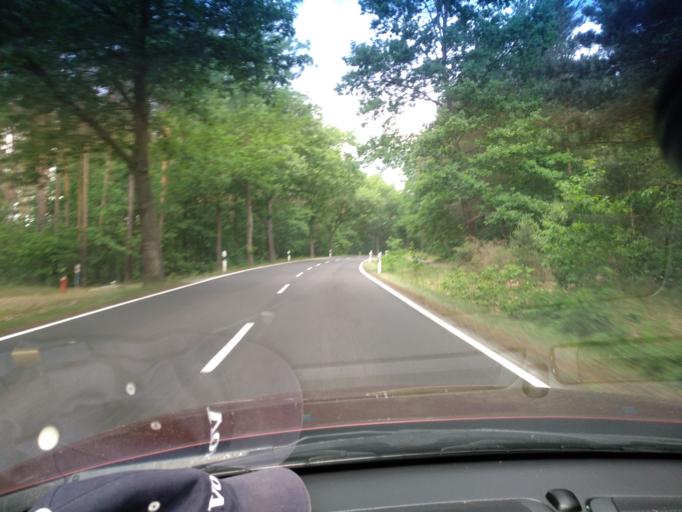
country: DE
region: Saxony
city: Mucka
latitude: 51.3378
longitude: 14.6868
